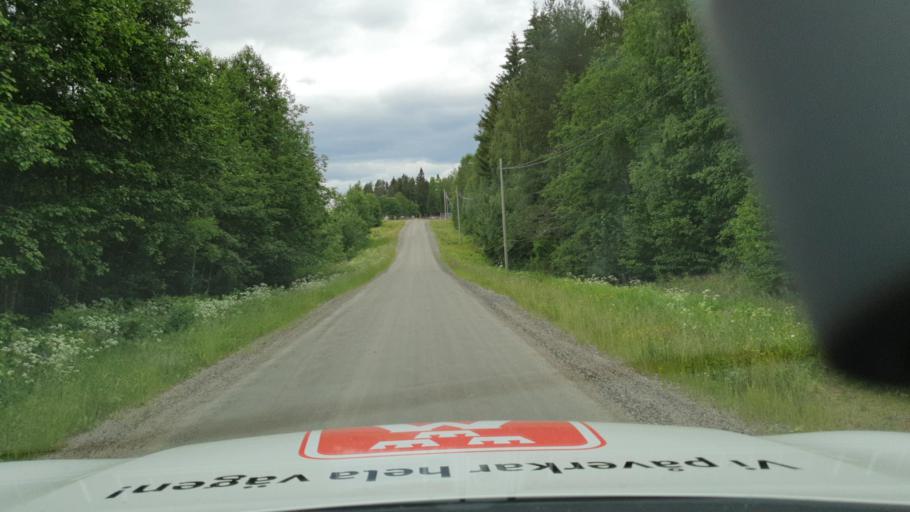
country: SE
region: Vaesterbotten
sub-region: Bjurholms Kommun
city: Bjurholm
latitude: 63.7342
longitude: 19.2969
